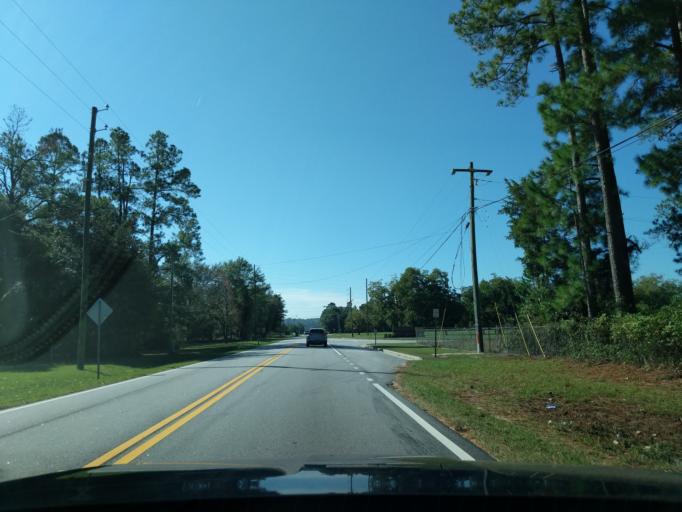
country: US
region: Georgia
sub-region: Richmond County
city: Hephzibah
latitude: 33.3566
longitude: -81.9982
